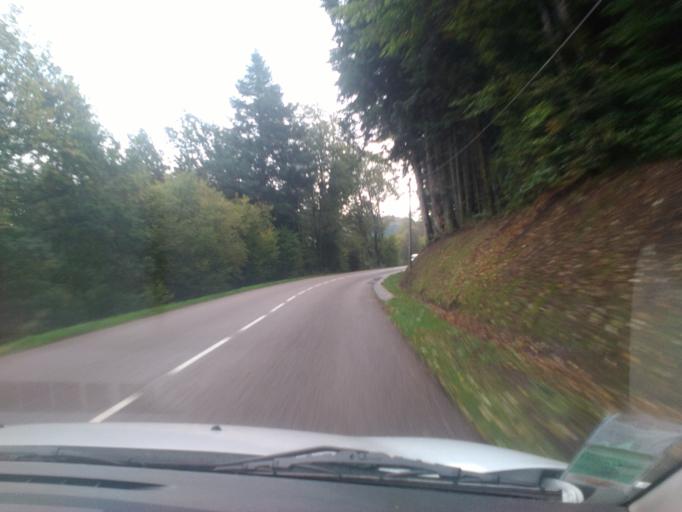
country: FR
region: Lorraine
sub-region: Departement des Vosges
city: Granges-sur-Vologne
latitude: 48.1892
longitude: 6.7904
